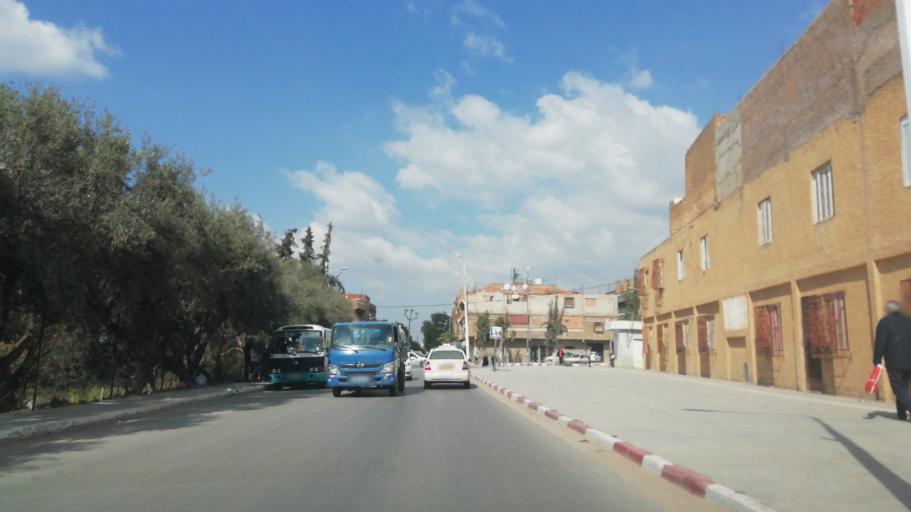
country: DZ
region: Mascara
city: Mascara
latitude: 35.5777
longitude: 0.0705
